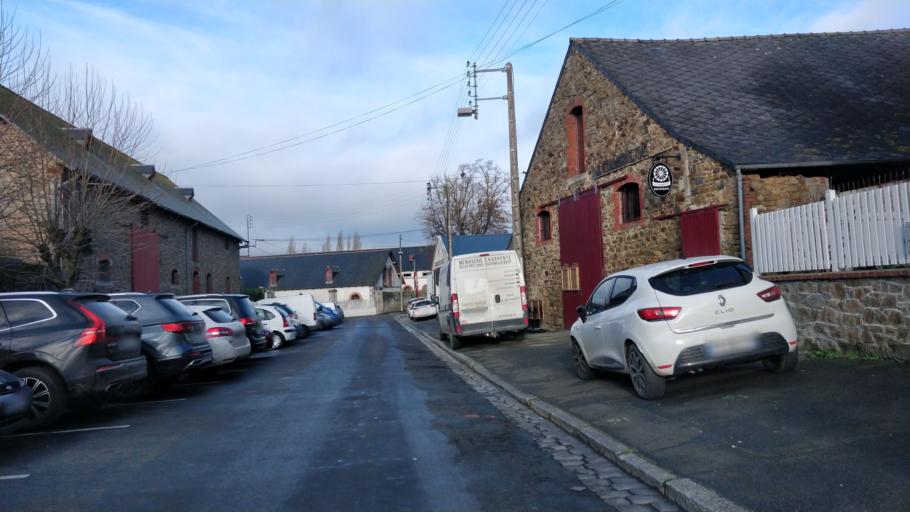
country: FR
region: Brittany
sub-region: Departement des Cotes-d'Armor
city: Lamballe
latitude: 48.4711
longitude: -2.5177
